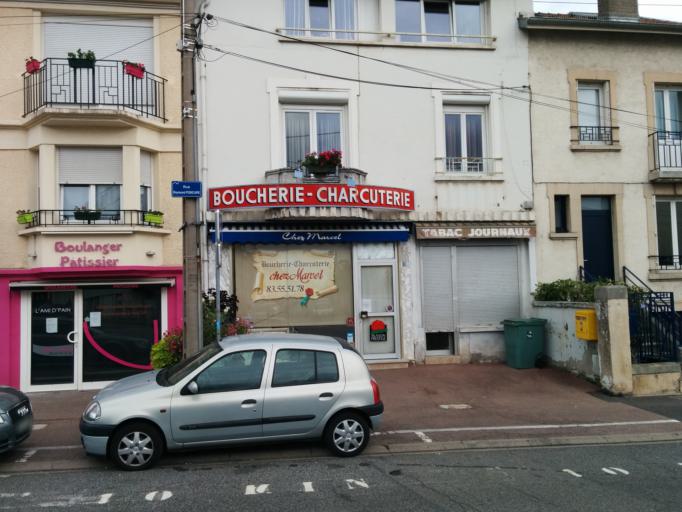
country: FR
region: Lorraine
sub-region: Departement de Meurthe-et-Moselle
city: Jarville-la-Malgrange
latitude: 48.6691
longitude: 6.1951
